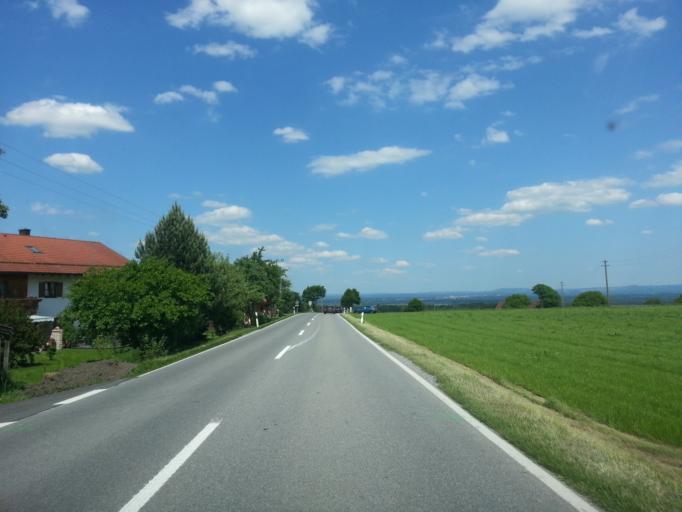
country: DE
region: Bavaria
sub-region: Upper Bavaria
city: Irschenberg
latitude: 47.8119
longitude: 11.9402
